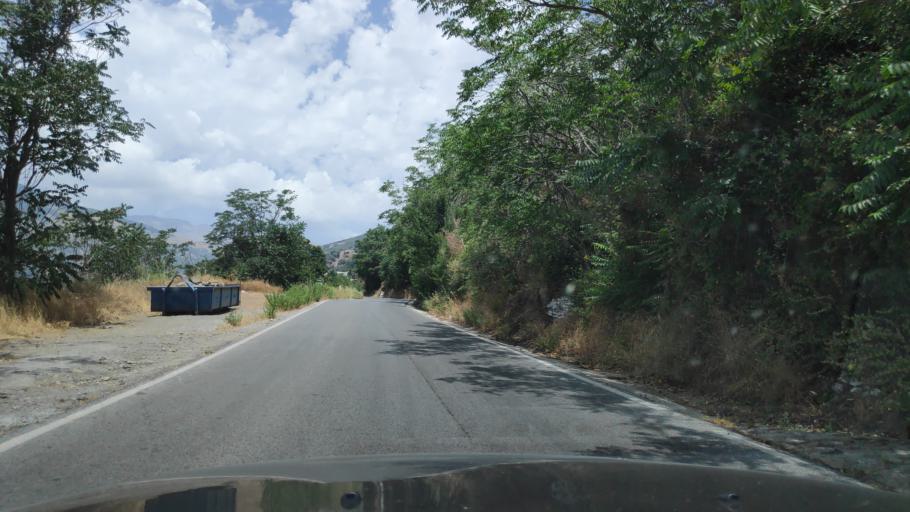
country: ES
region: Andalusia
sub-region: Provincia de Granada
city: Bubion
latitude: 36.9431
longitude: -3.3547
